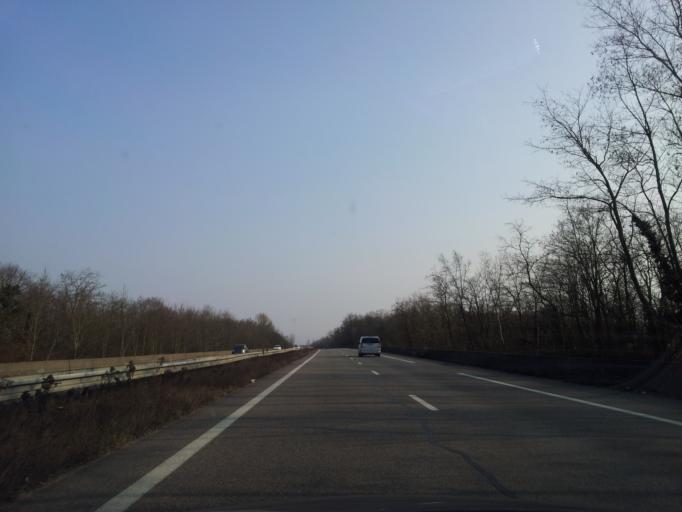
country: FR
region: Alsace
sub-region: Departement du Haut-Rhin
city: Blotzheim
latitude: 47.6228
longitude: 7.5100
